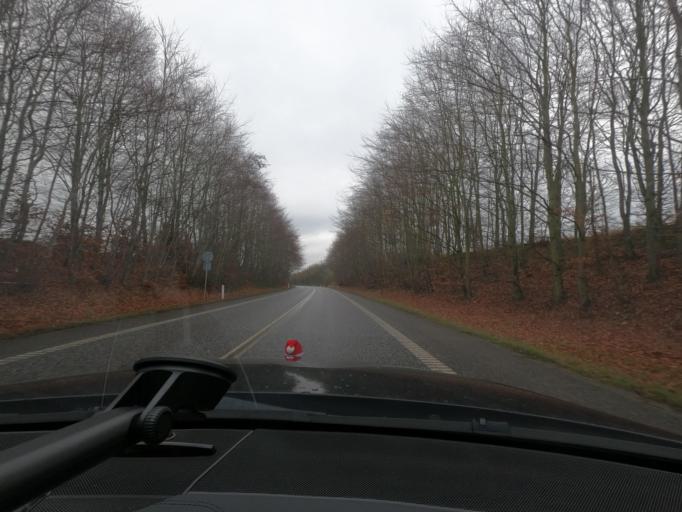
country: DK
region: South Denmark
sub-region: Sonderborg Kommune
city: Horuphav
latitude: 54.9117
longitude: 9.9141
